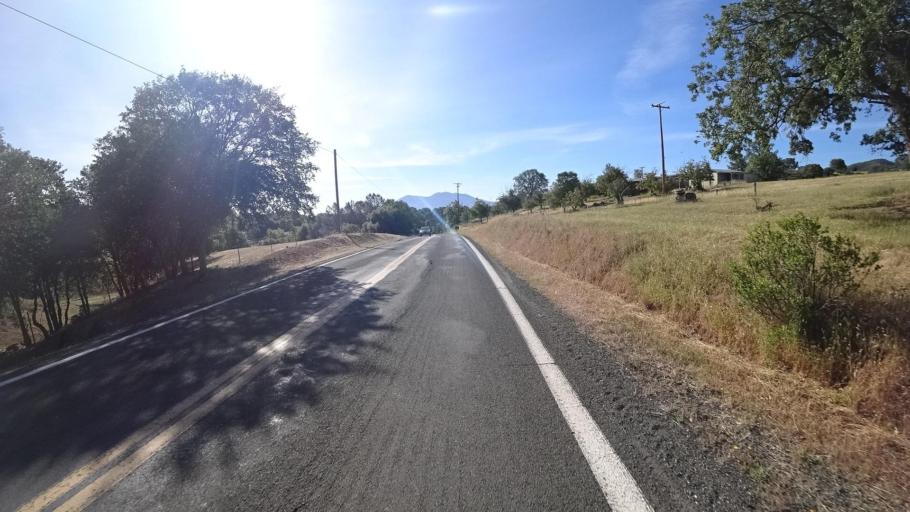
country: US
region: California
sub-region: Lake County
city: Lakeport
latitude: 39.0415
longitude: -122.9454
